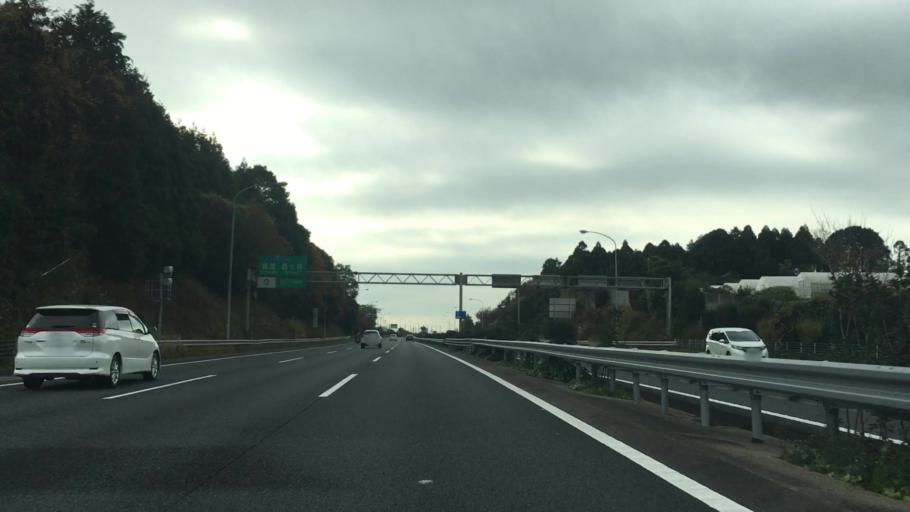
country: JP
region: Chiba
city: Narita
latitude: 35.7568
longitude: 140.3200
